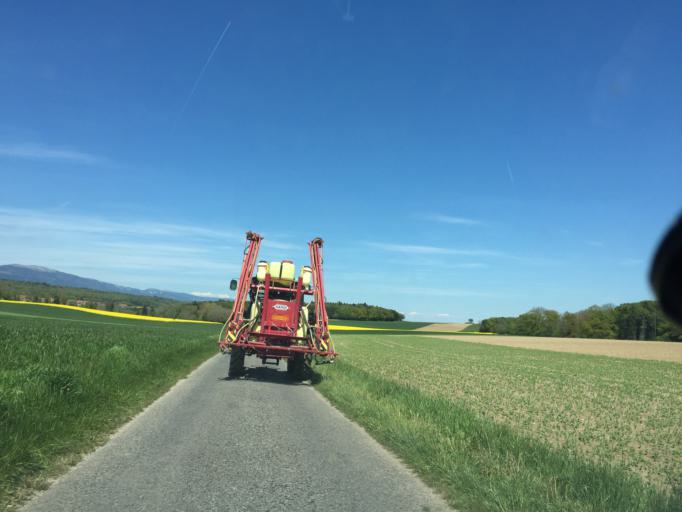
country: CH
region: Vaud
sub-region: Morges District
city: Cuarnens
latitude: 46.6320
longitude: 6.4513
